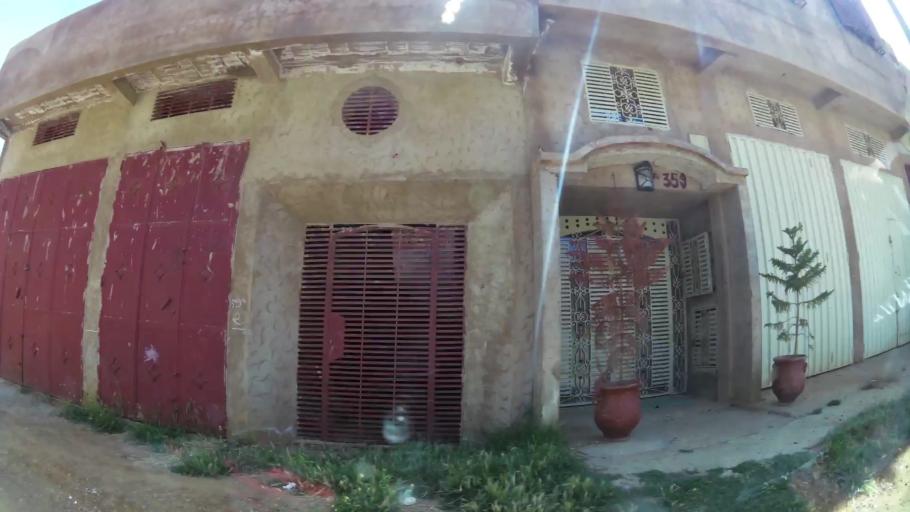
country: MA
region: Rabat-Sale-Zemmour-Zaer
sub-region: Khemisset
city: Khemisset
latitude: 33.8091
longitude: -6.0851
